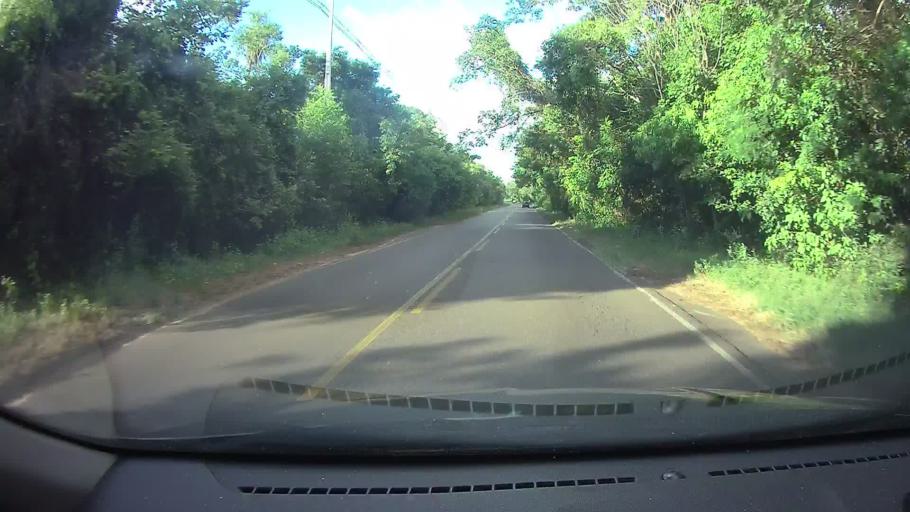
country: PY
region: Cordillera
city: Altos
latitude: -25.2267
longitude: -57.2266
